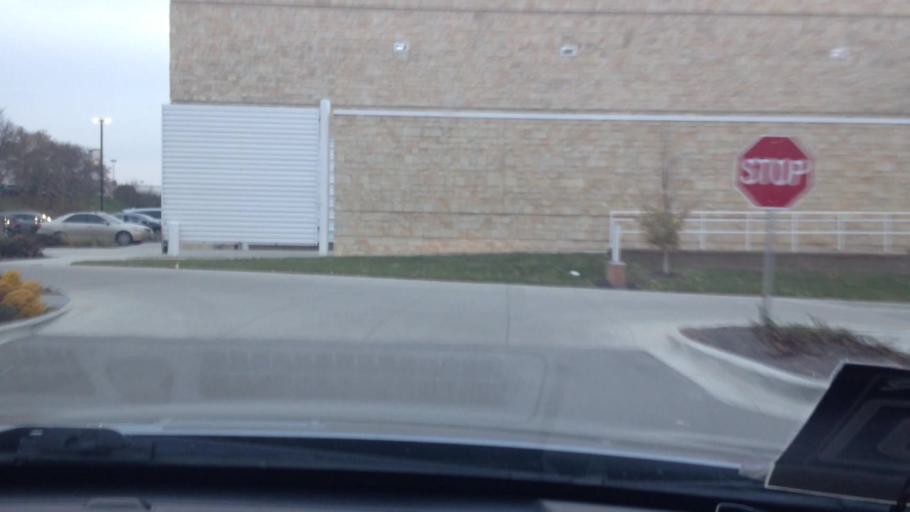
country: US
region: Kansas
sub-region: Johnson County
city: Leawood
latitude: 38.9118
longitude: -94.6405
